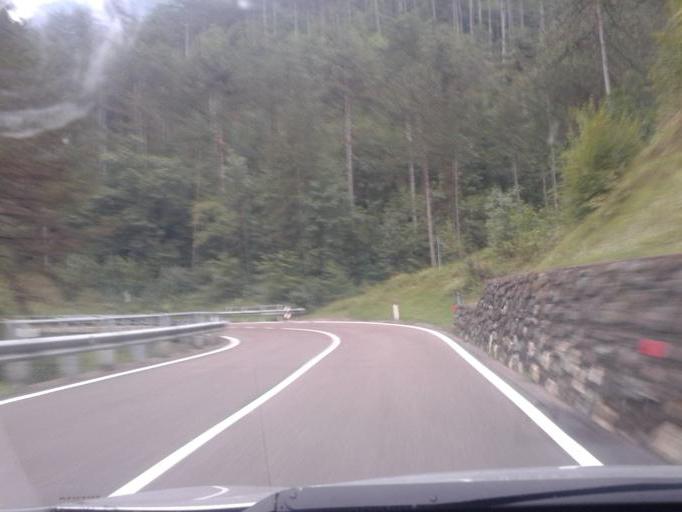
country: IT
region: Trentino-Alto Adige
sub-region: Provincia di Trento
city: Storo
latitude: 45.8404
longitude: 10.5897
